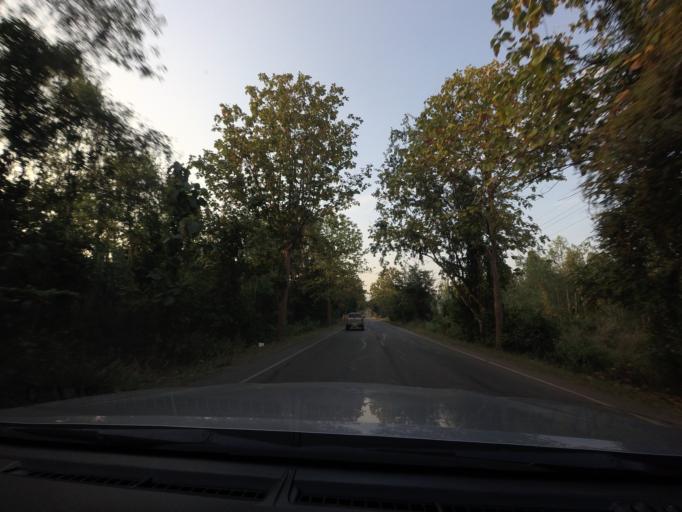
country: TH
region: Phitsanulok
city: Wang Thong
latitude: 16.6988
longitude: 100.5174
